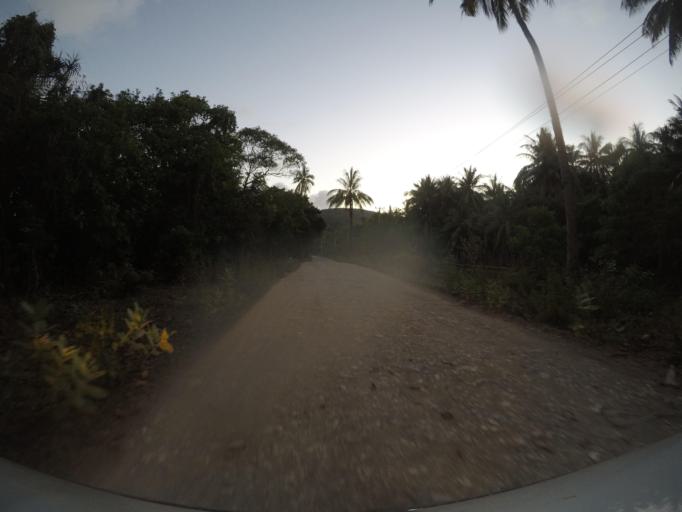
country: TL
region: Viqueque
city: Viqueque
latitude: -8.7878
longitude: 126.6313
